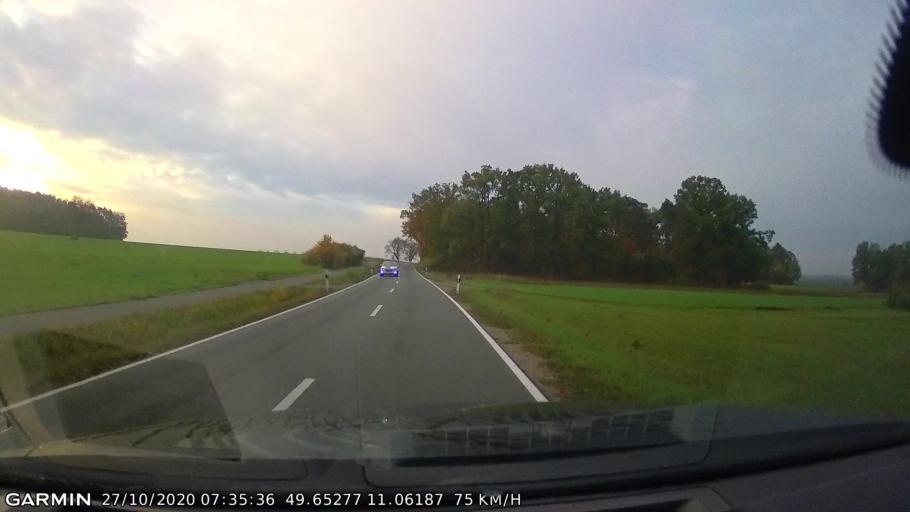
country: DE
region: Bavaria
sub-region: Upper Franconia
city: Poxdorf
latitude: 49.6524
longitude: 11.0622
